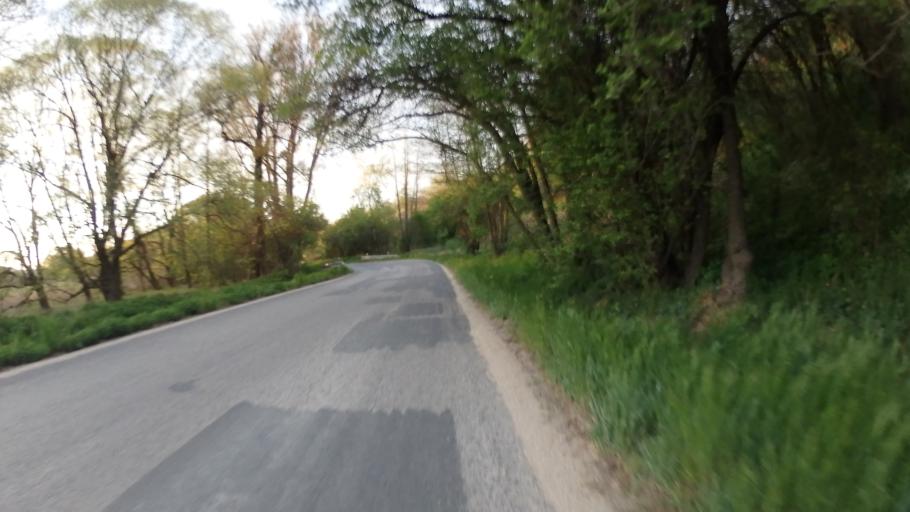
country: CZ
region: South Moravian
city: Strelice
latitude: 49.1476
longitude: 16.4654
